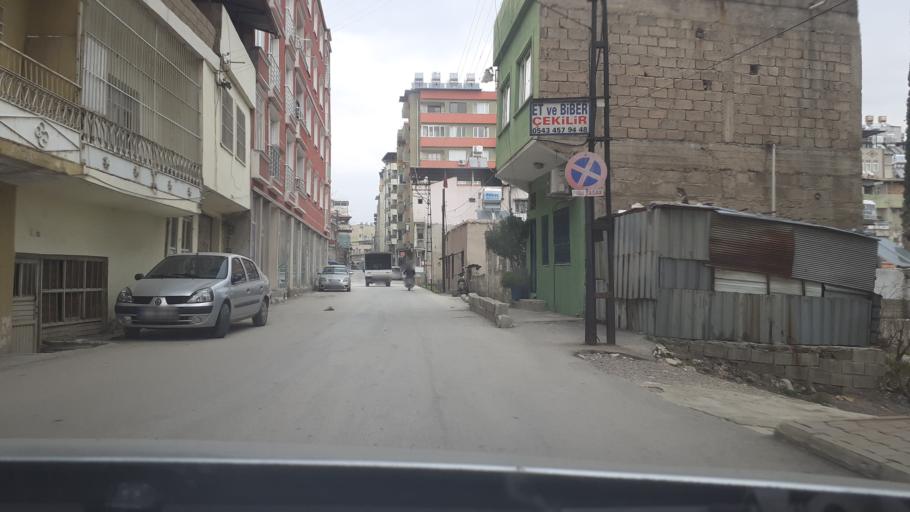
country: TR
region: Hatay
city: Kirikhan
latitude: 36.4967
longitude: 36.3537
